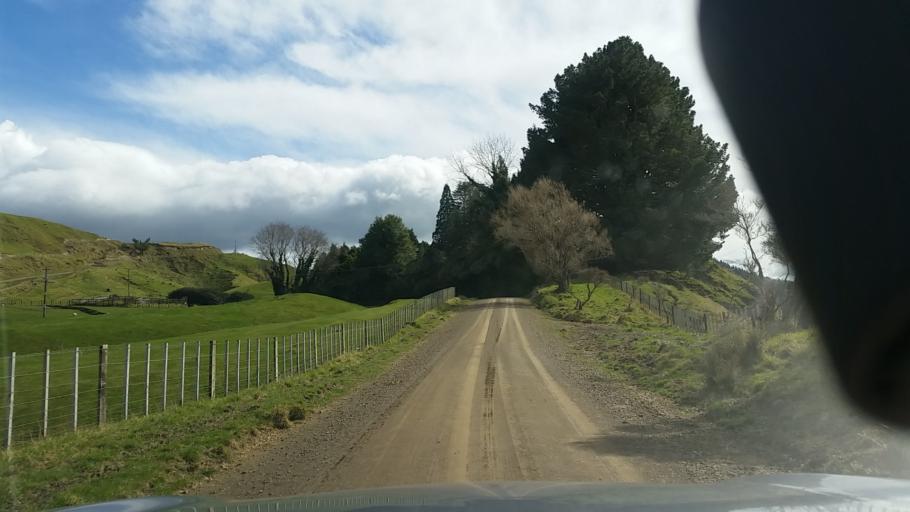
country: NZ
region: Hawke's Bay
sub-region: Napier City
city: Napier
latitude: -39.2123
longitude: 176.9696
